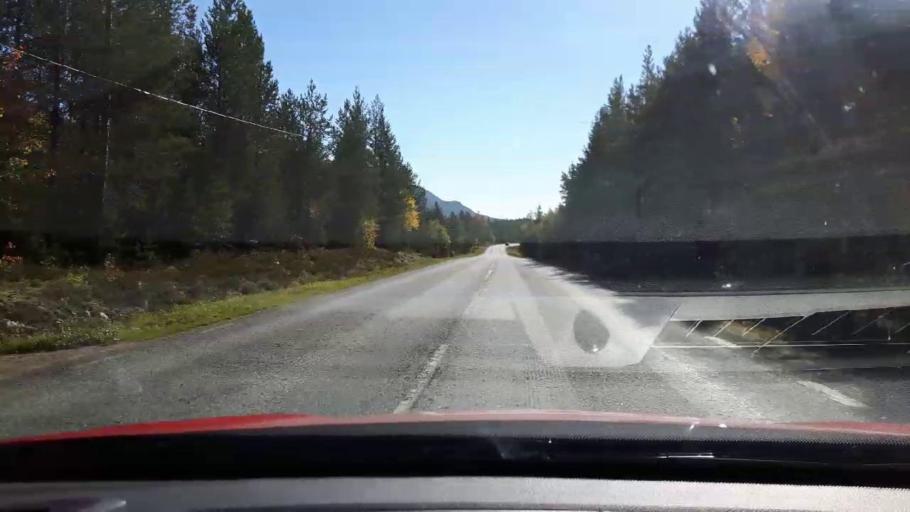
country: SE
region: Jaemtland
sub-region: Harjedalens Kommun
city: Sveg
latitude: 62.4321
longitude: 13.8857
